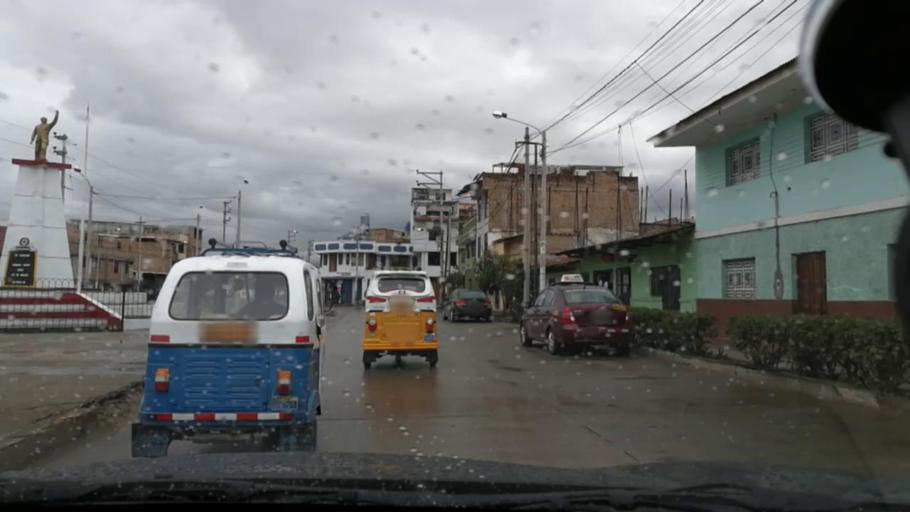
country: PE
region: Cajamarca
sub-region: Provincia de Cajamarca
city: Cajamarca
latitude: -7.1612
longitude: -78.5073
